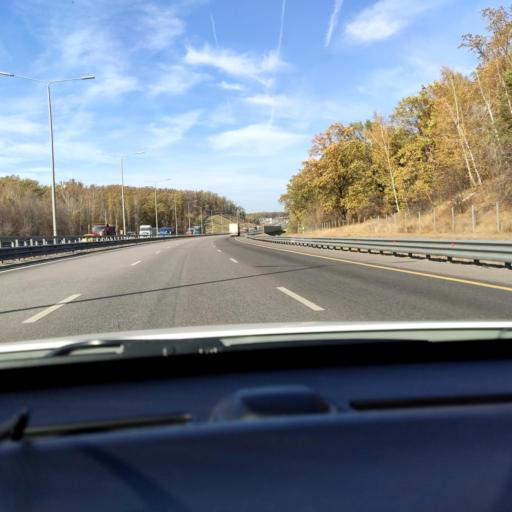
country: RU
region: Voronezj
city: Podgornoye
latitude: 51.7994
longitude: 39.2558
